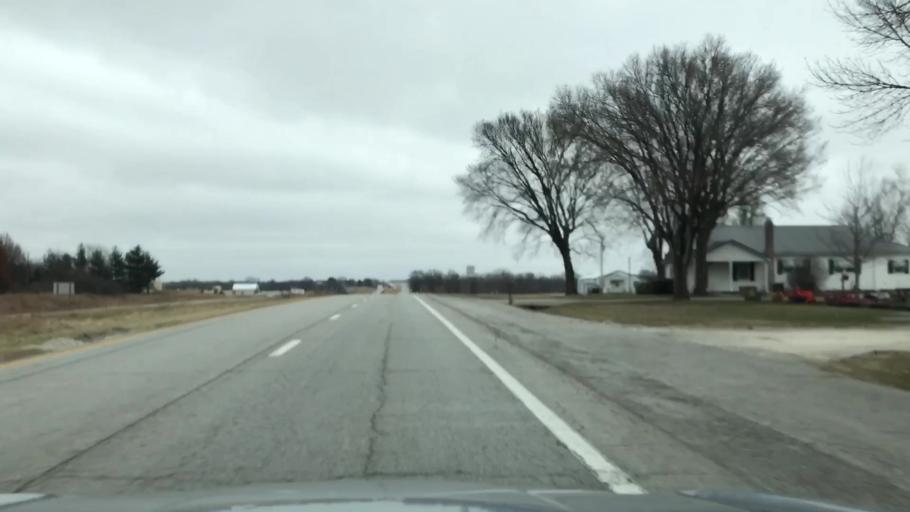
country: US
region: Missouri
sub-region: Linn County
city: Brookfield
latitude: 39.7784
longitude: -93.1729
